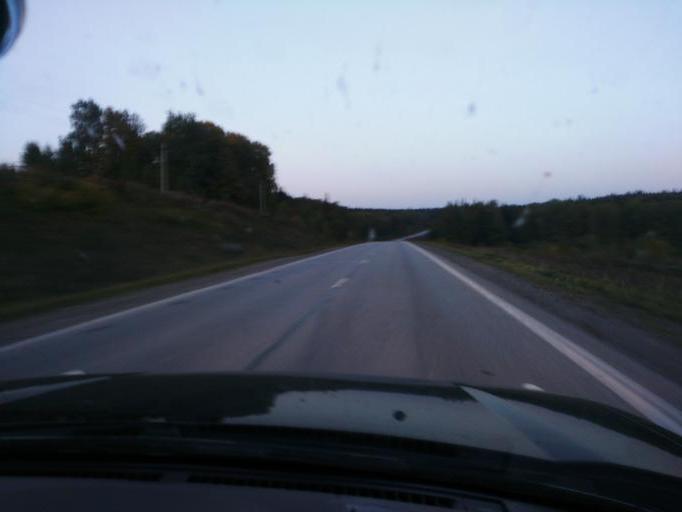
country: RU
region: Perm
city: Verkhnechusovskiye Gorodki
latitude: 58.2811
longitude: 56.9118
